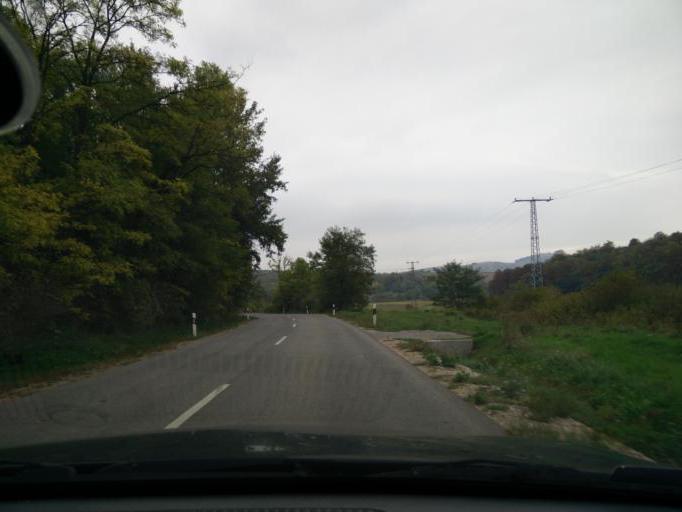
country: HU
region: Komarom-Esztergom
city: Bajna
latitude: 47.6975
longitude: 18.6168
